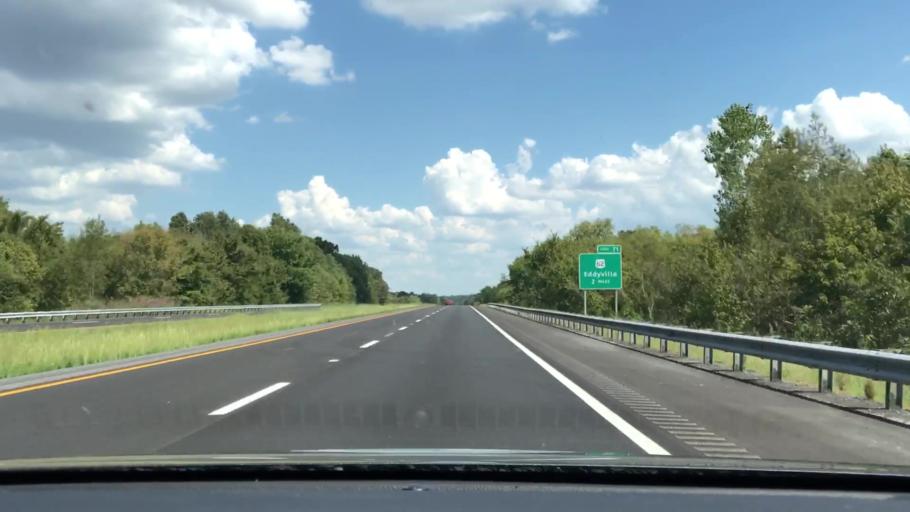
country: US
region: Kentucky
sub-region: Lyon County
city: Eddyville
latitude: 37.0848
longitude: -88.0664
